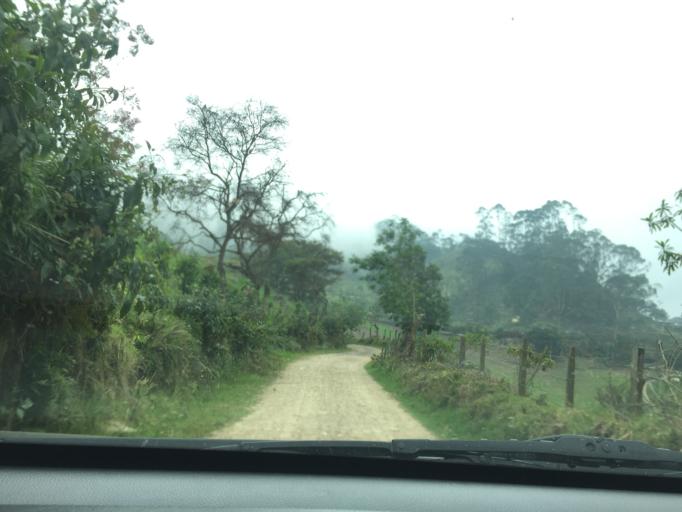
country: CO
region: Cundinamarca
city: Bojaca
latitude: 4.7047
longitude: -74.3607
